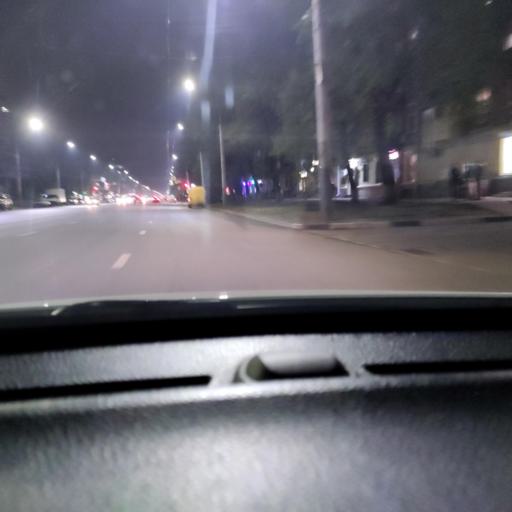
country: RU
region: Voronezj
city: Voronezh
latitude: 51.6419
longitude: 39.2370
